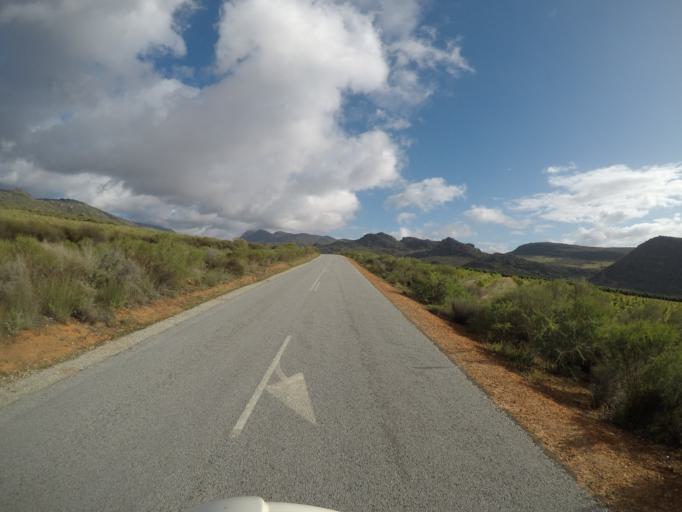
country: ZA
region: Western Cape
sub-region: West Coast District Municipality
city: Clanwilliam
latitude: -32.4284
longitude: 18.9376
